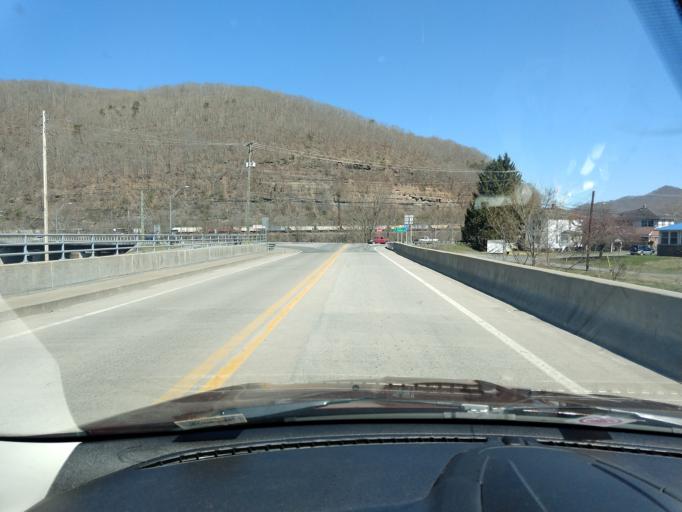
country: US
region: West Virginia
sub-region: Summers County
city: Hinton
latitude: 37.6515
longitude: -80.8856
